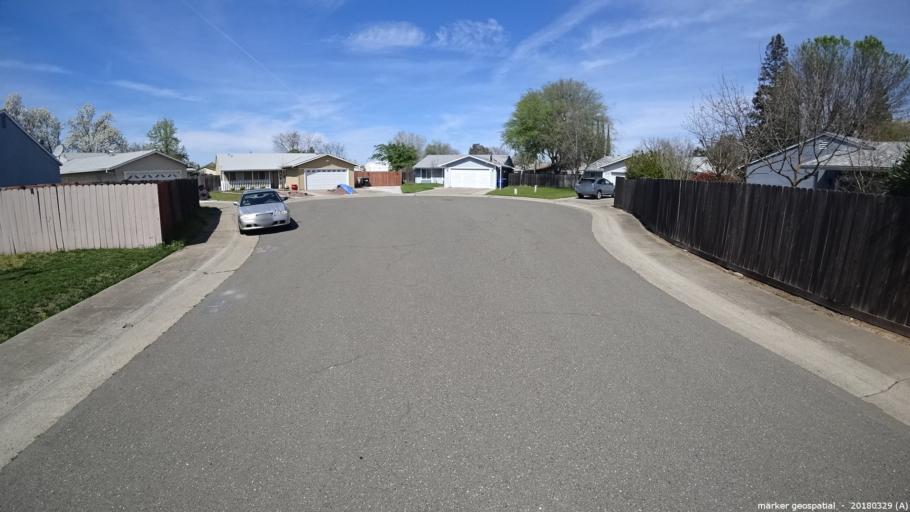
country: US
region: California
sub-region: Sacramento County
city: Rosemont
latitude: 38.5447
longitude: -121.3513
